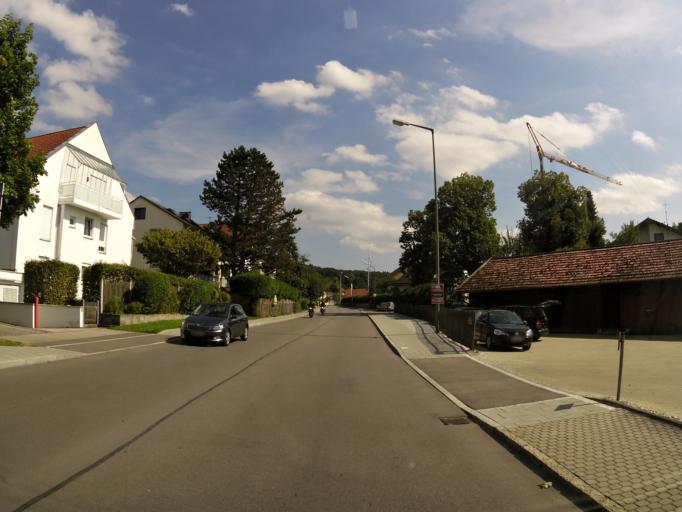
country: DE
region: Bavaria
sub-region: Upper Bavaria
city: Herrsching am Ammersee
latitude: 48.0008
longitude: 11.1728
